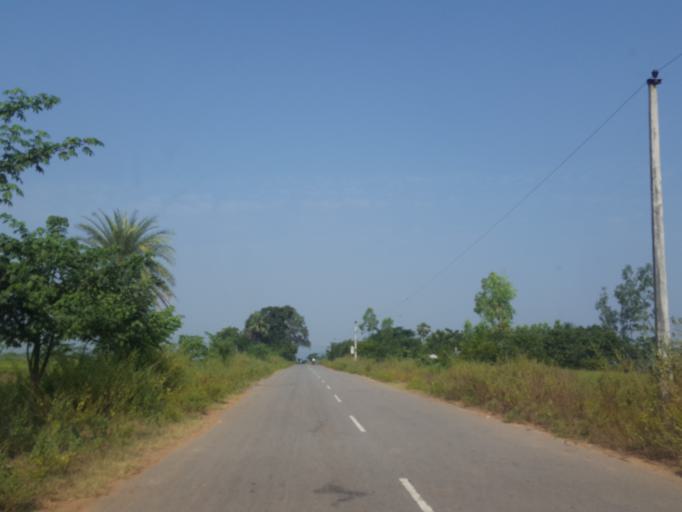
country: IN
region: Telangana
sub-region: Khammam
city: Yellandu
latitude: 17.6471
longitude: 80.2919
